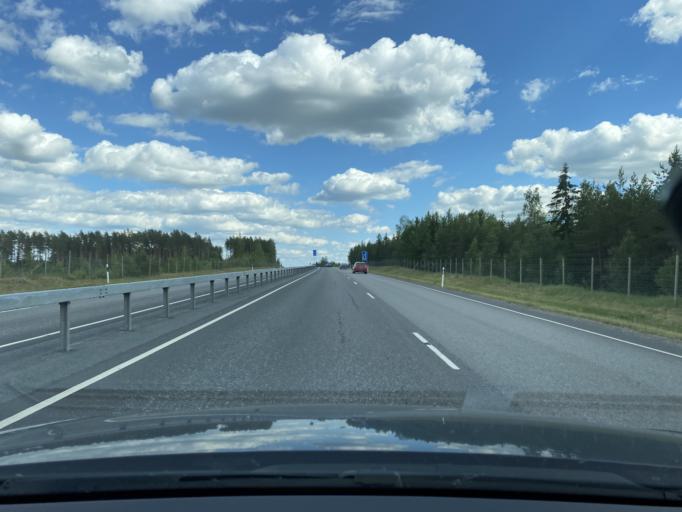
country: FI
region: Varsinais-Suomi
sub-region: Loimaa
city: Alastaro
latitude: 61.0533
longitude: 22.9549
